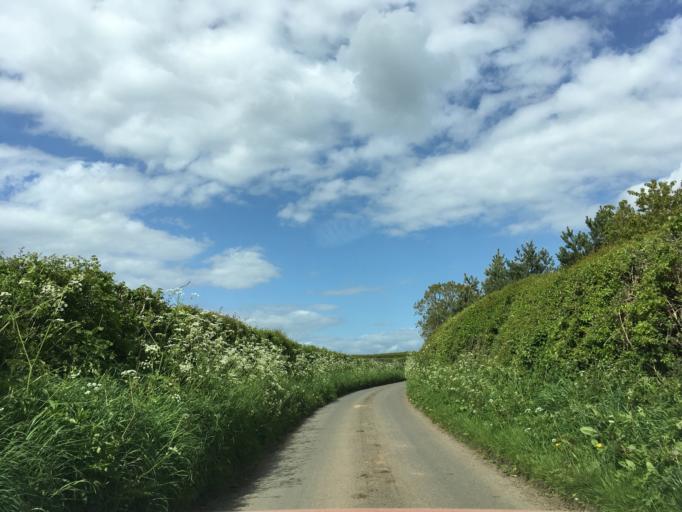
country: GB
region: England
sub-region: South Gloucestershire
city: Charfield
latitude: 51.6423
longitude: -2.3945
